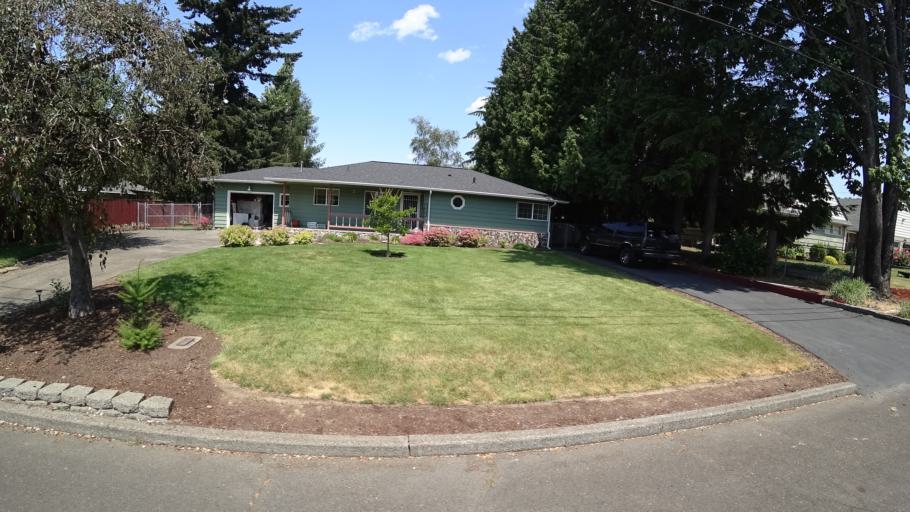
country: US
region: Oregon
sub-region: Multnomah County
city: Lents
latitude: 45.4627
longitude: -122.5670
